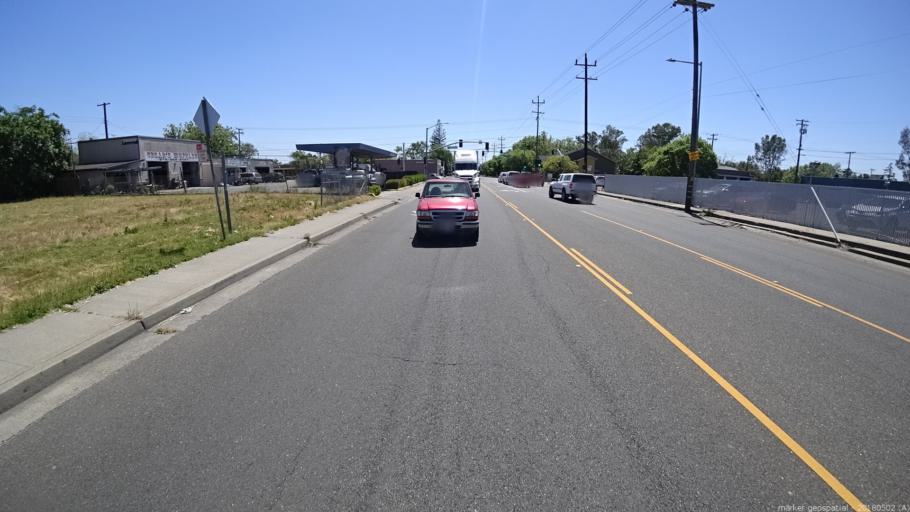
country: US
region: California
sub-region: Sacramento County
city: Rio Linda
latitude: 38.6374
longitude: -121.4461
